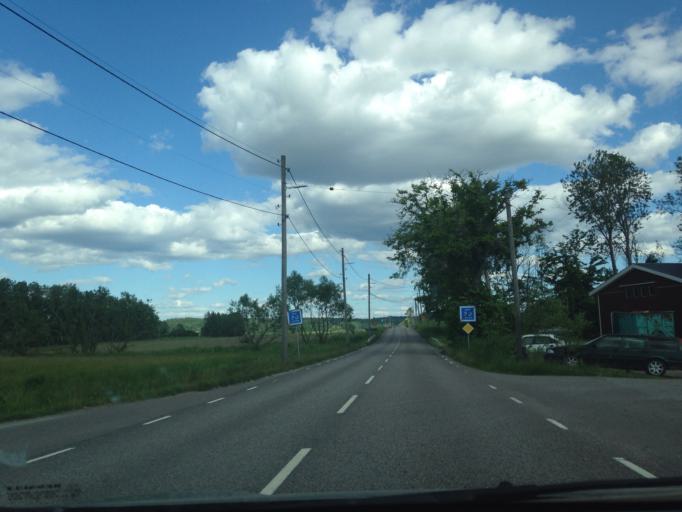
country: SE
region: Vaestra Goetaland
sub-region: Goteborg
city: Majorna
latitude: 57.7732
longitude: 11.9123
